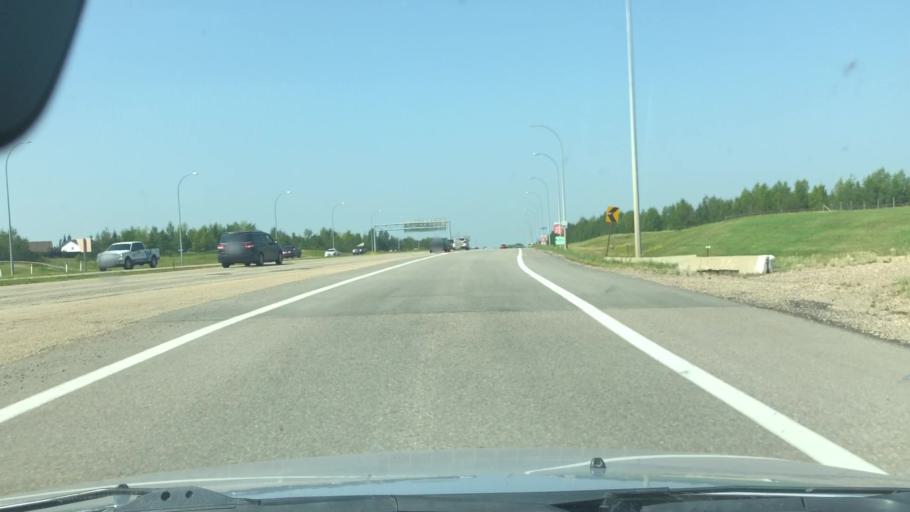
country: CA
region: Alberta
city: St. Albert
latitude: 53.5122
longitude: -113.6638
